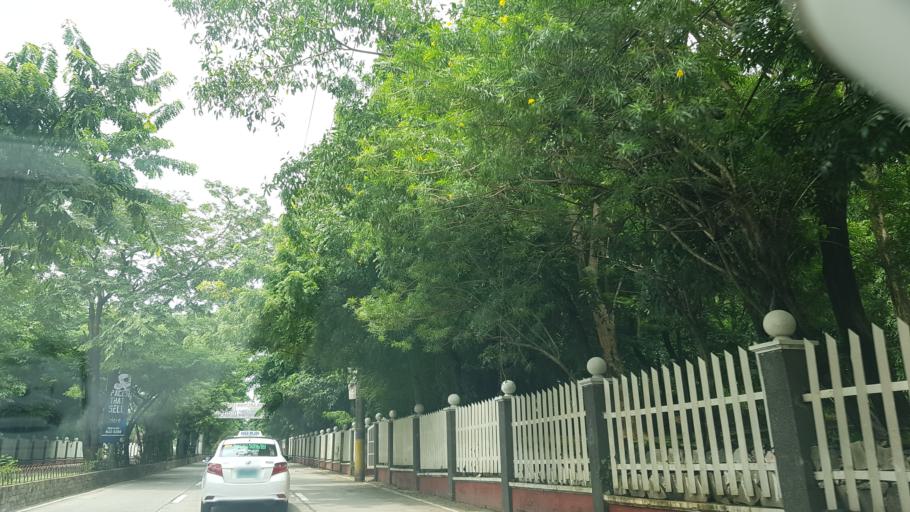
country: PH
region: Metro Manila
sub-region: Makati City
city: Makati City
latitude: 14.5318
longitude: 121.0410
